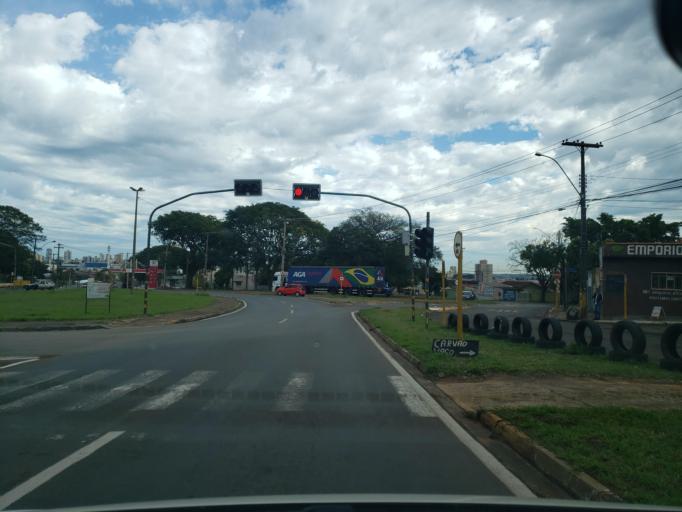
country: BR
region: Sao Paulo
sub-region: Bauru
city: Bauru
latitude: -22.3353
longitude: -49.0311
